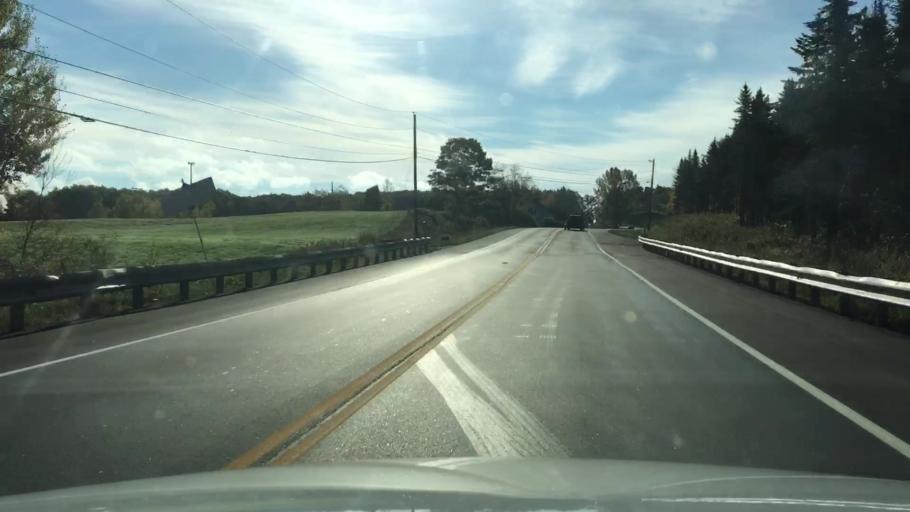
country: US
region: Maine
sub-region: Knox County
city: Warren
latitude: 44.0968
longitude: -69.2432
